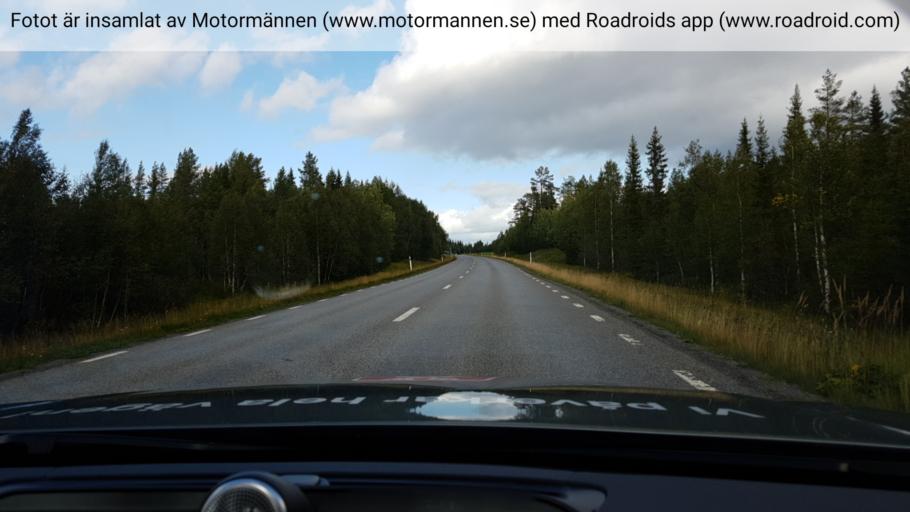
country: SE
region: Jaemtland
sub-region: OEstersunds Kommun
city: Lit
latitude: 63.4288
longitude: 15.1187
